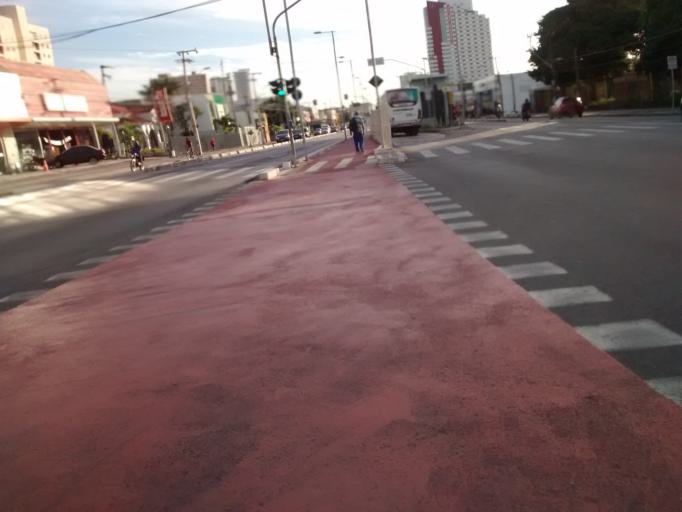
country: BR
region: Ceara
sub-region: Fortaleza
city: Fortaleza
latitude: -3.7331
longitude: -38.5521
